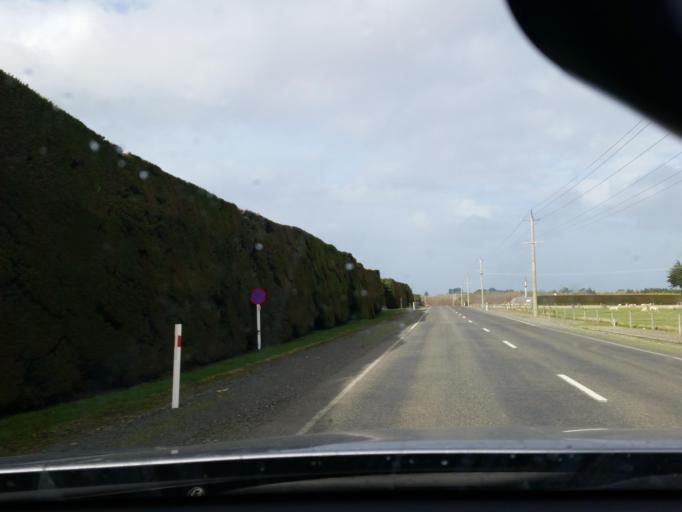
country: NZ
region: Southland
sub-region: Invercargill City
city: Invercargill
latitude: -46.3033
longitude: 168.3233
